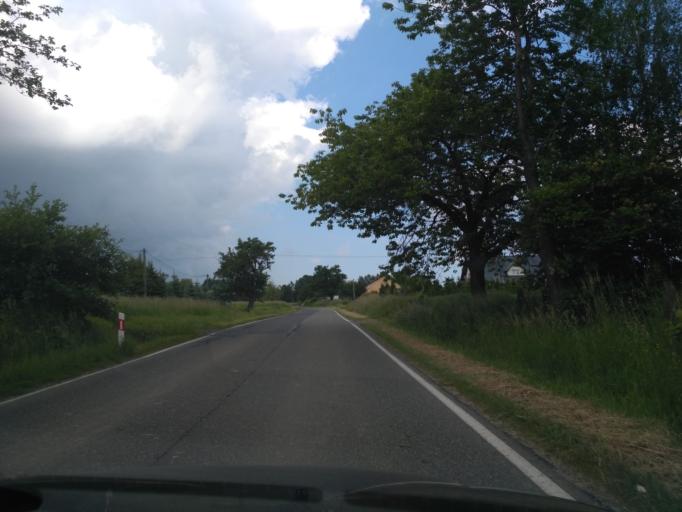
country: PL
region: Subcarpathian Voivodeship
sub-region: Powiat lancucki
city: Handzlowka
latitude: 49.9601
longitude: 22.1973
